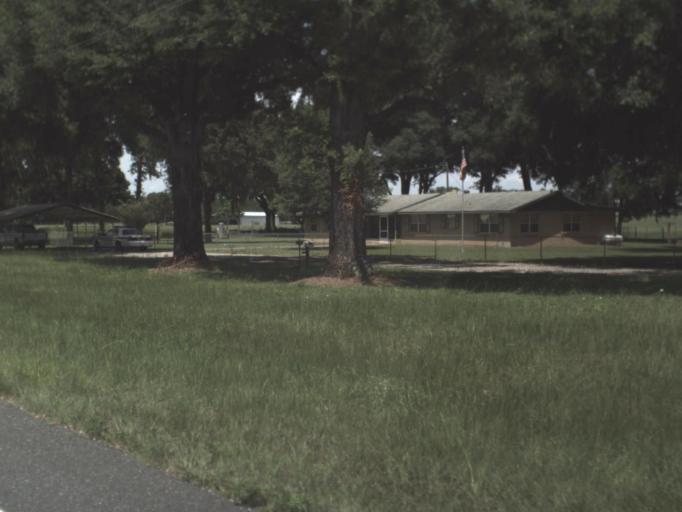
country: US
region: Florida
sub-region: Gilchrist County
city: Trenton
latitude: 29.8407
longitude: -82.8662
